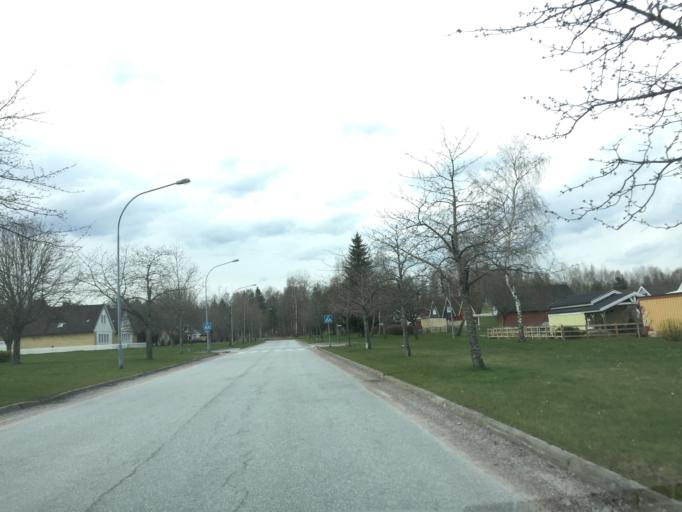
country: SE
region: OErebro
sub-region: Orebro Kommun
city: Orebro
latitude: 59.3127
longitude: 15.1810
